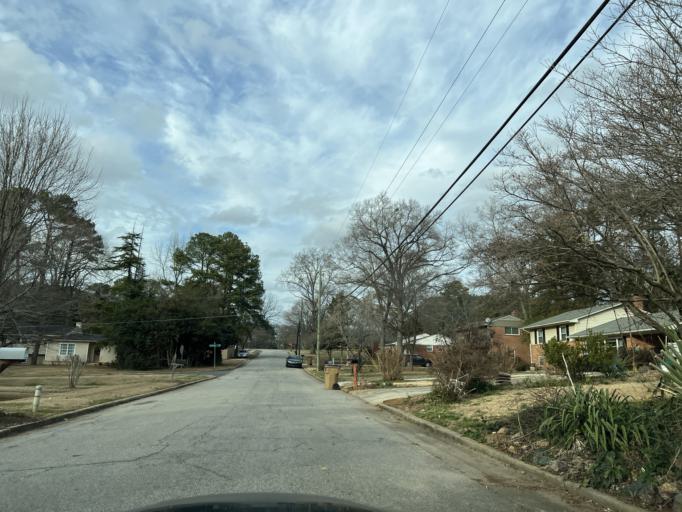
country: US
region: North Carolina
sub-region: Wake County
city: West Raleigh
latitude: 35.7758
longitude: -78.7048
